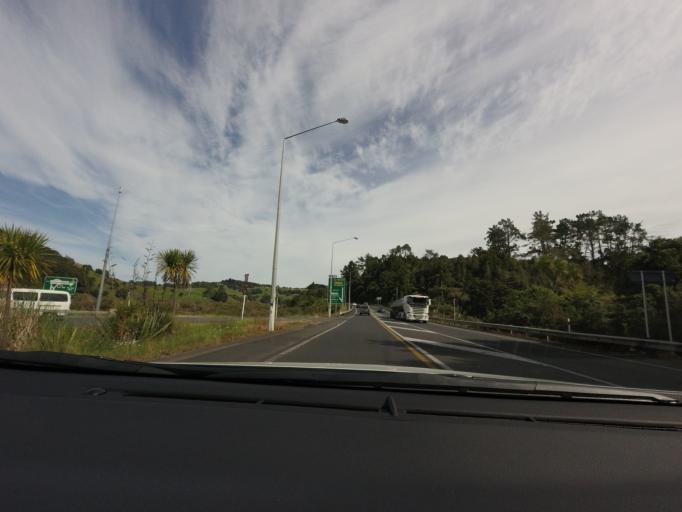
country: NZ
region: Auckland
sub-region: Auckland
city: Warkworth
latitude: -36.5228
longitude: 174.6758
